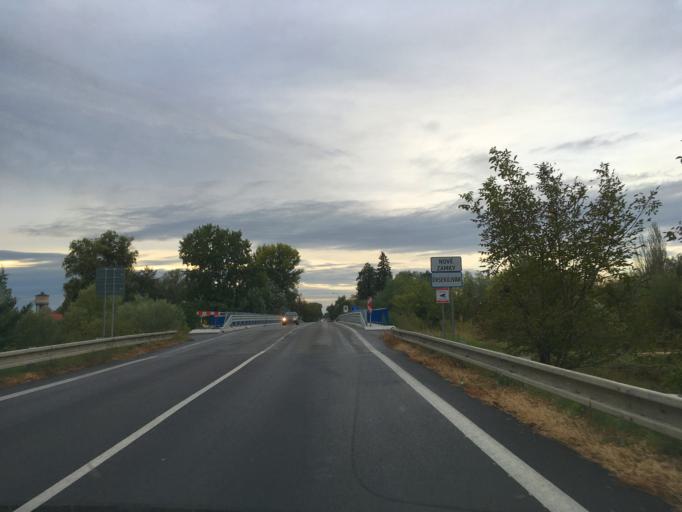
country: SK
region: Nitriansky
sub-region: Okres Nove Zamky
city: Nove Zamky
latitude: 47.9960
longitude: 18.1864
